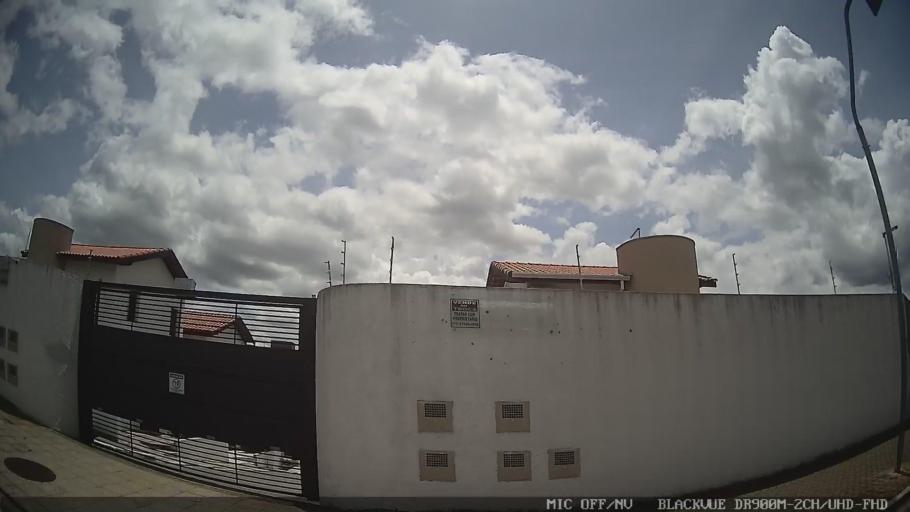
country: BR
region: Sao Paulo
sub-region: Mogi das Cruzes
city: Mogi das Cruzes
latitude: -23.5392
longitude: -46.2032
